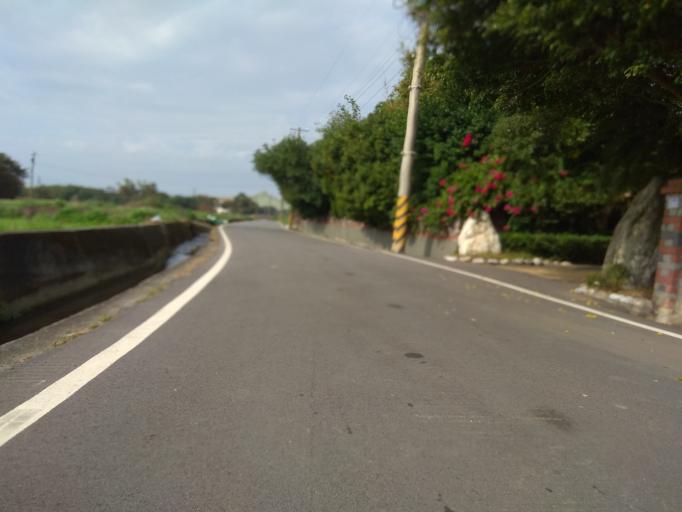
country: TW
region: Taiwan
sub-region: Hsinchu
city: Zhubei
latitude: 24.9811
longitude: 121.0303
